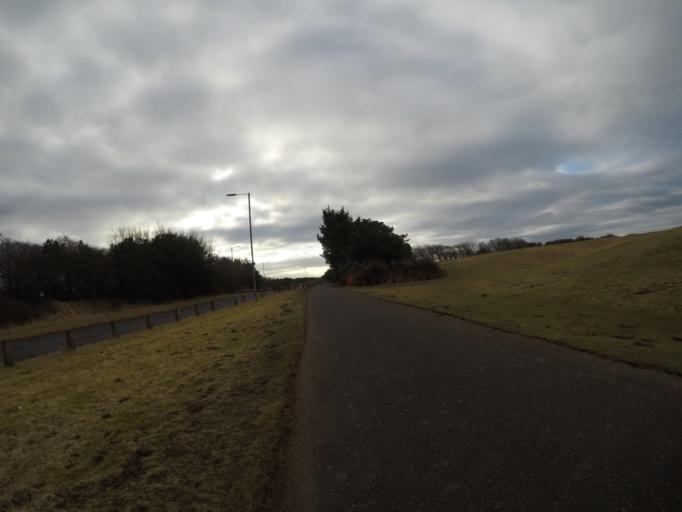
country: GB
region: Scotland
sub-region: North Ayrshire
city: Irvine
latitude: 55.6021
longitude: -4.6807
